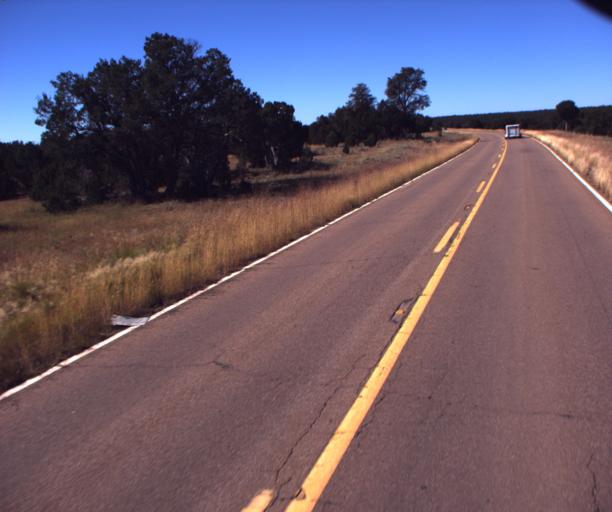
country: US
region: Arizona
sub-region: Navajo County
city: Heber-Overgaard
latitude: 34.4601
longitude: -110.5073
